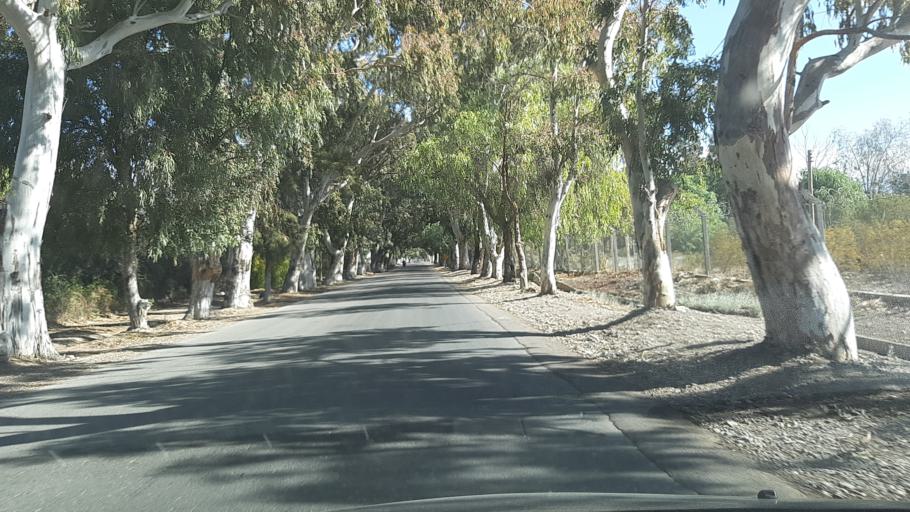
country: AR
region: San Juan
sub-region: Departamento de Zonda
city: Zonda
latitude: -31.5462
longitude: -68.7239
